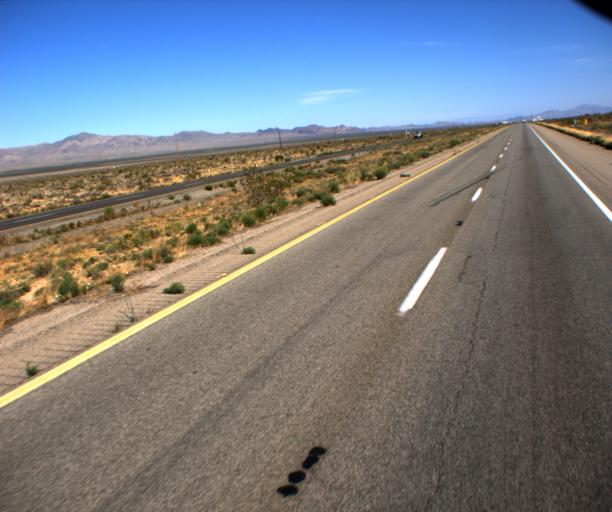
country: US
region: Arizona
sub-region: Mohave County
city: Dolan Springs
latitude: 35.5188
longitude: -114.3447
